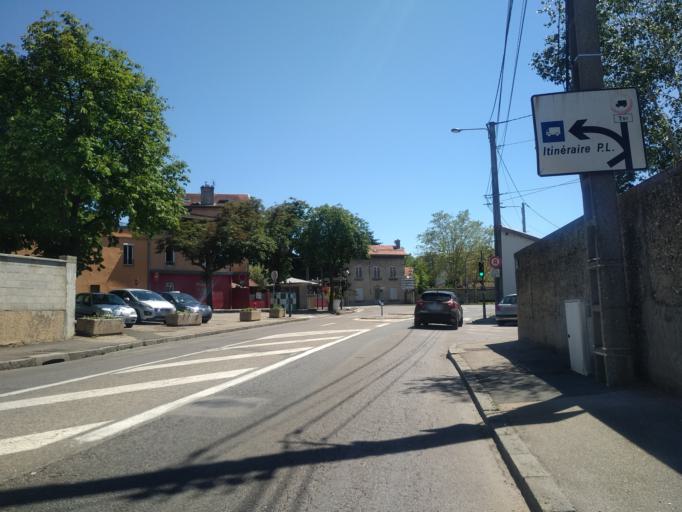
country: FR
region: Rhone-Alpes
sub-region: Departement du Rhone
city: Sathonay-Camp
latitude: 45.8163
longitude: 4.8629
